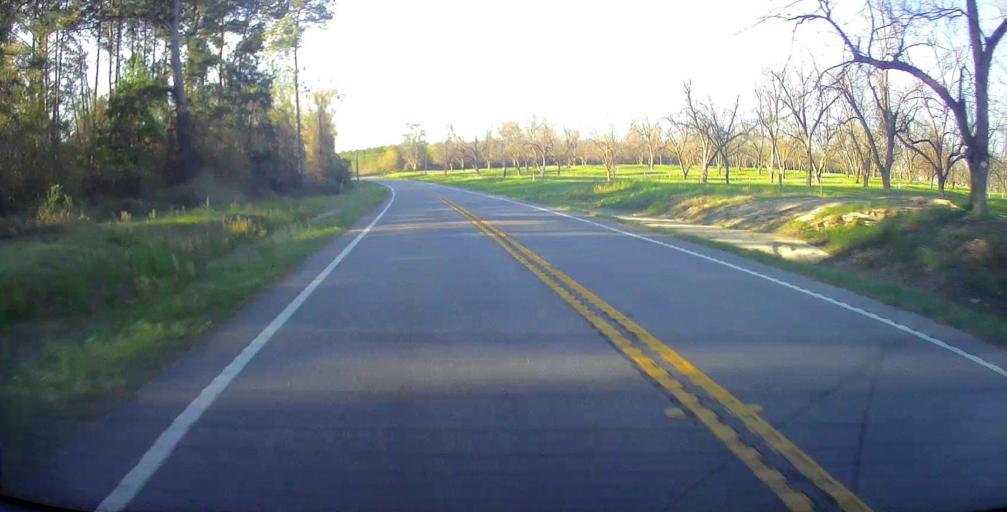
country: US
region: Georgia
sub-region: Wilcox County
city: Abbeville
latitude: 32.0333
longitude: -83.2521
